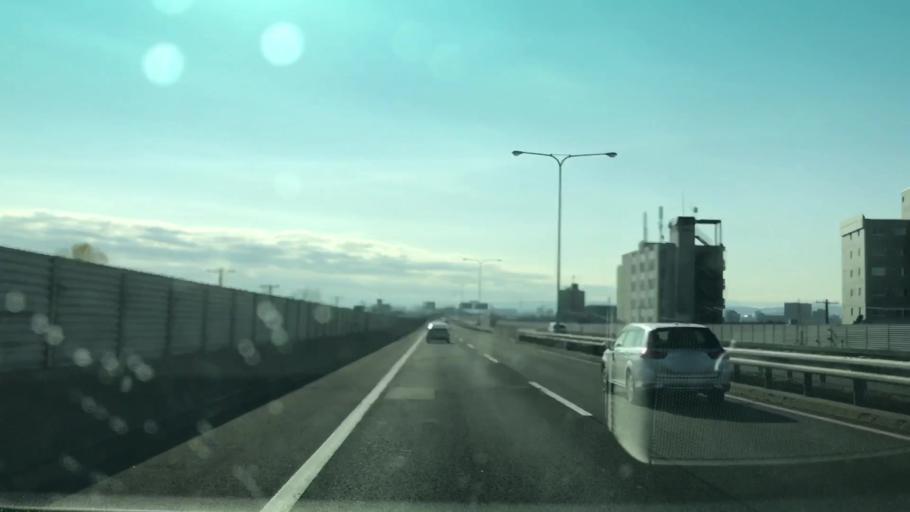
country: JP
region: Hokkaido
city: Sapporo
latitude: 43.0683
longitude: 141.4228
